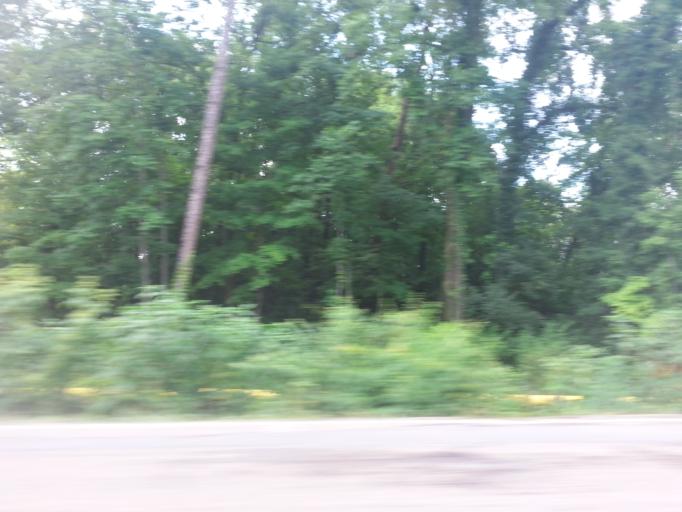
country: US
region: Tennessee
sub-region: Blount County
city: Louisville
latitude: 35.9110
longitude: -84.0066
